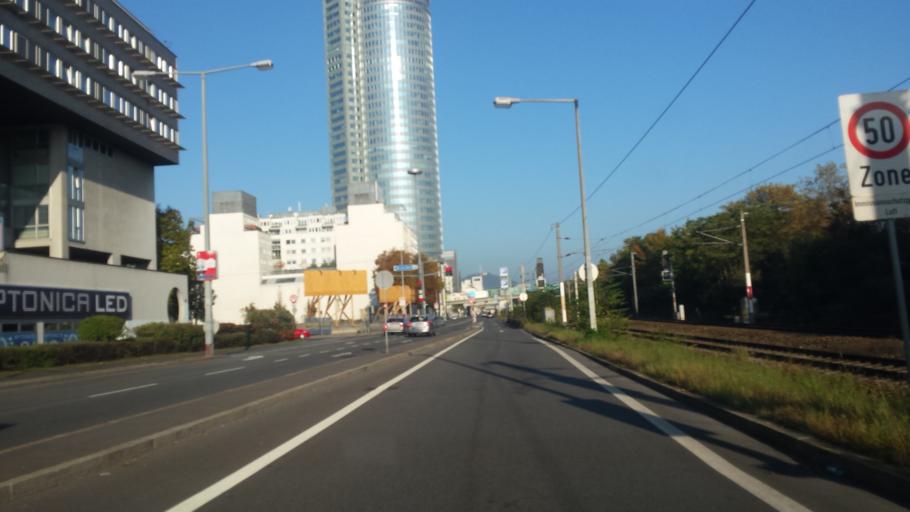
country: AT
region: Vienna
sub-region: Wien Stadt
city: Vienna
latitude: 48.2384
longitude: 16.3897
